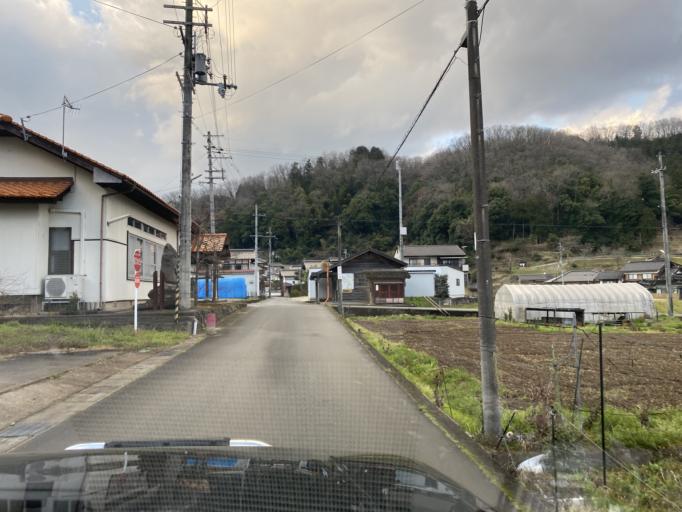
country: JP
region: Hyogo
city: Toyooka
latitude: 35.4725
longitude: 134.7681
